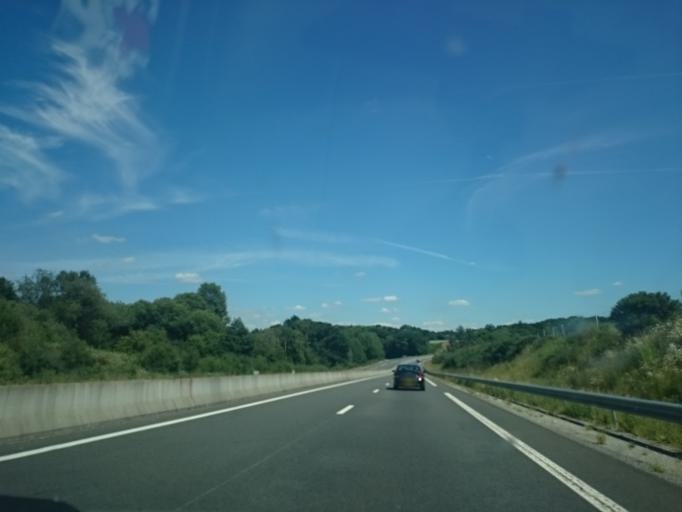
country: FR
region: Brittany
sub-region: Departement des Cotes-d'Armor
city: Gouarec
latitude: 48.2283
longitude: -3.1165
